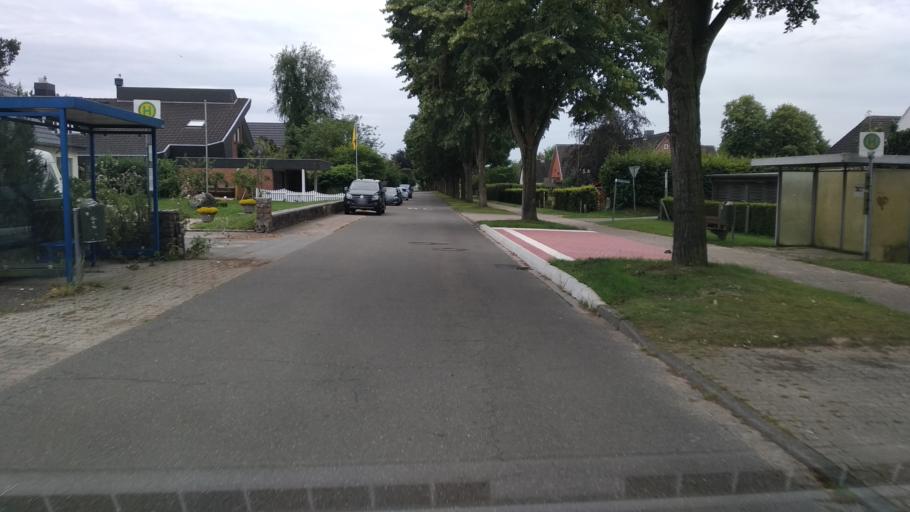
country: DE
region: Schleswig-Holstein
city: Schuby
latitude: 54.5241
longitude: 9.4825
